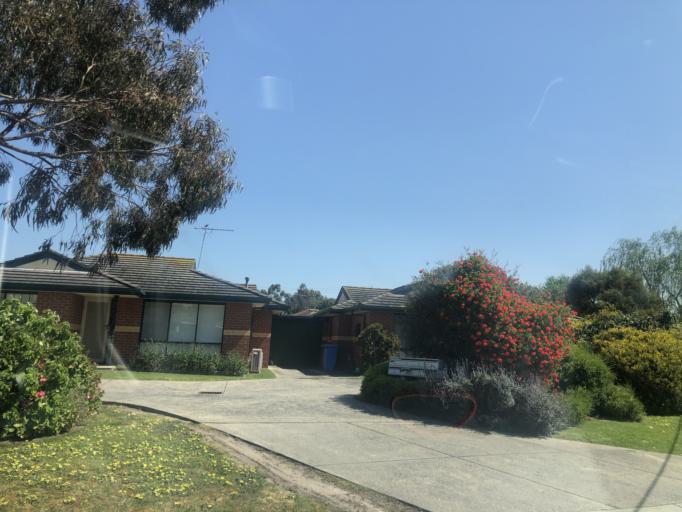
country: AU
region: Victoria
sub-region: Casey
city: Narre Warren South
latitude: -38.0348
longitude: 145.2813
